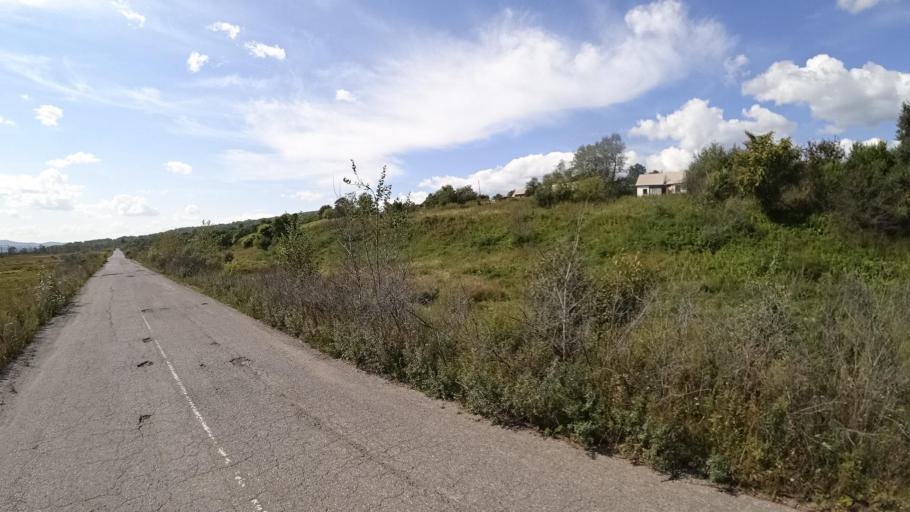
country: RU
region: Jewish Autonomous Oblast
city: Londoko
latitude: 49.0033
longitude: 131.8700
